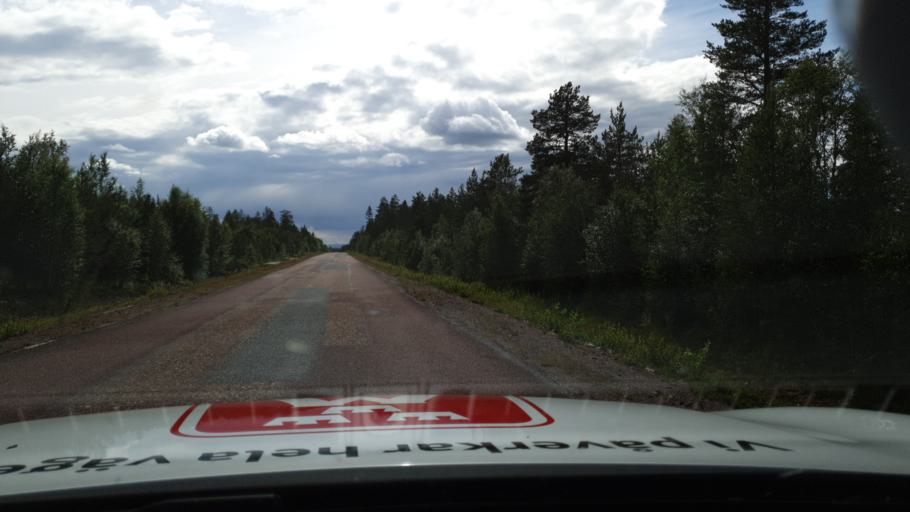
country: SE
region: Dalarna
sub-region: Alvdalens Kommun
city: AElvdalen
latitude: 61.7657
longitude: 13.4741
